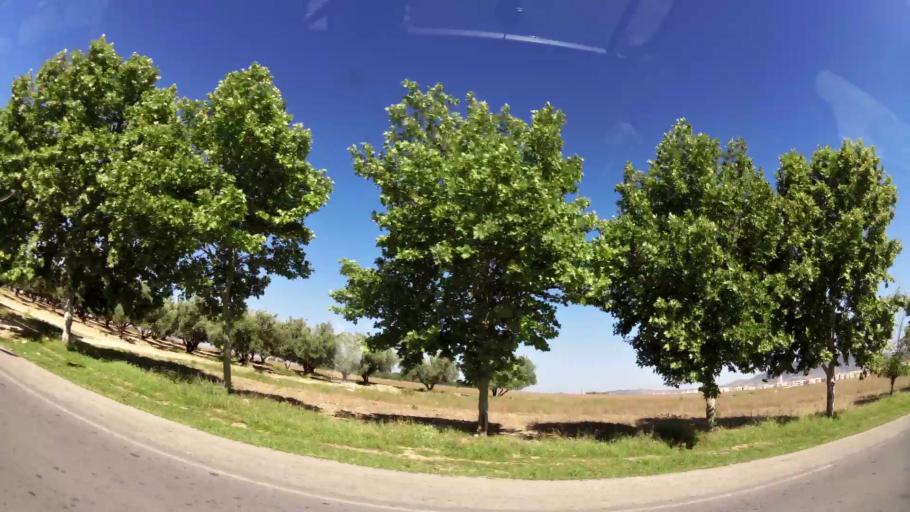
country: MA
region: Fes-Boulemane
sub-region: Fes
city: Fes
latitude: 34.0012
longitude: -5.0238
